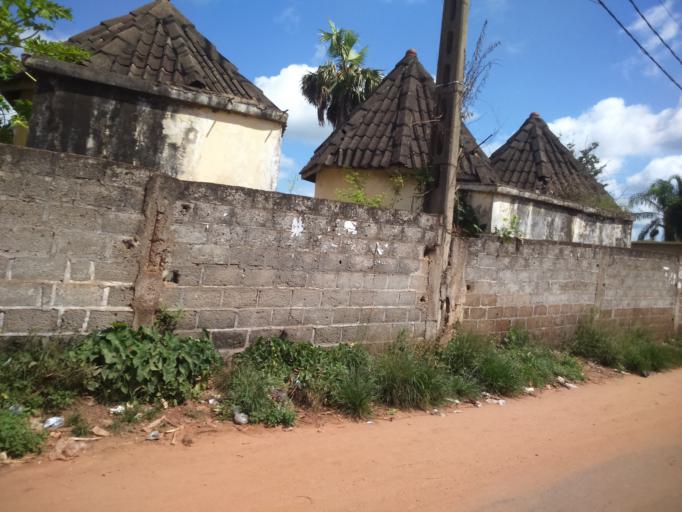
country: CI
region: Agneby
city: Agboville
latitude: 5.9285
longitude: -4.2184
